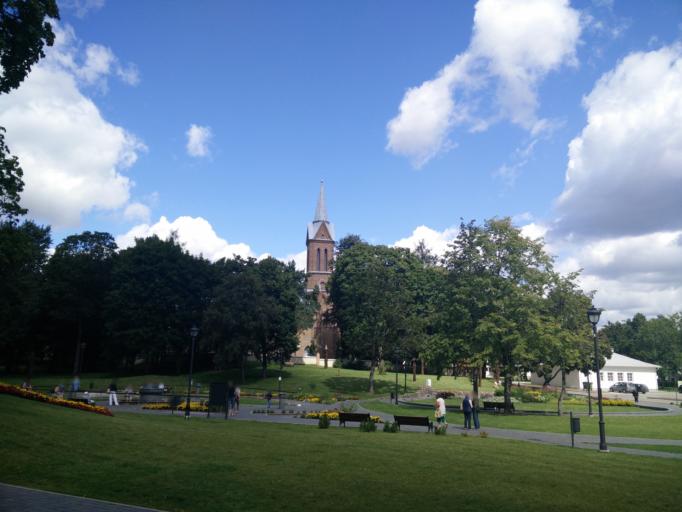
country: LT
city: Birstonas
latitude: 54.6004
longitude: 24.0341
